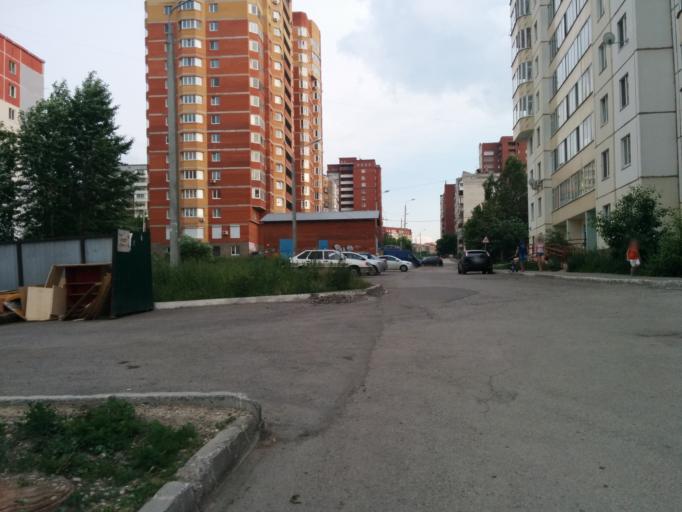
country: RU
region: Perm
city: Perm
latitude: 58.0103
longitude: 56.3034
